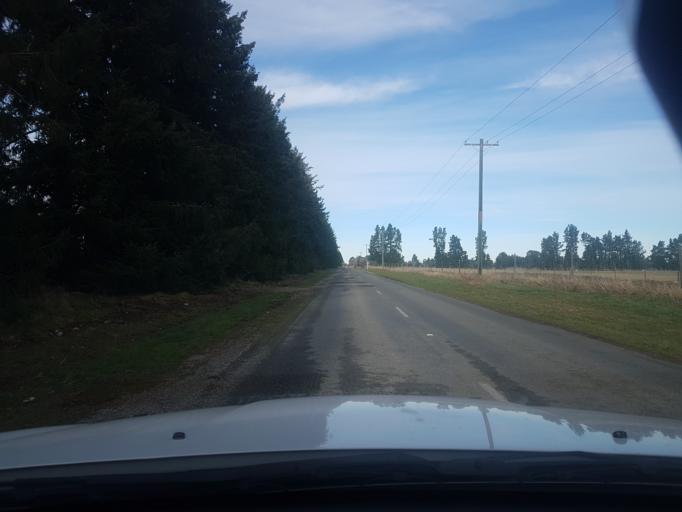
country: NZ
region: Canterbury
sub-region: Timaru District
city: Pleasant Point
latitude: -43.9580
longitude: 171.2648
